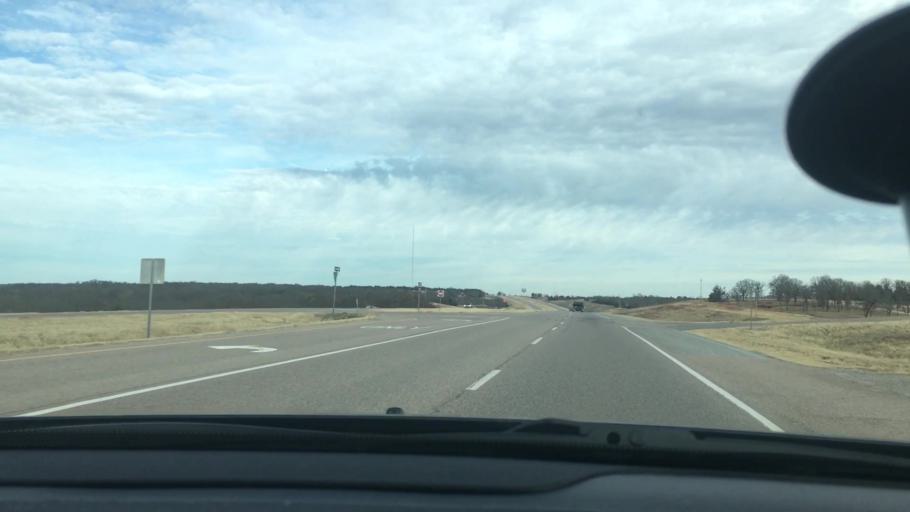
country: US
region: Oklahoma
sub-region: Pontotoc County
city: Byng
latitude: 34.8752
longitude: -96.6774
